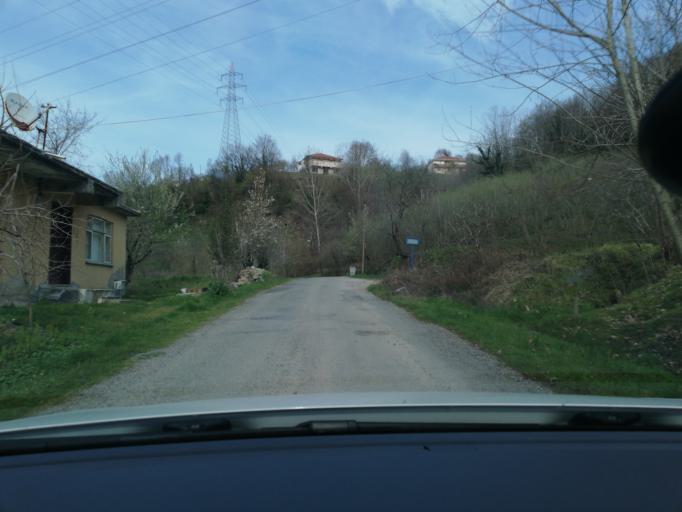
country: TR
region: Zonguldak
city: Kozlu
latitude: 41.3584
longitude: 31.6321
